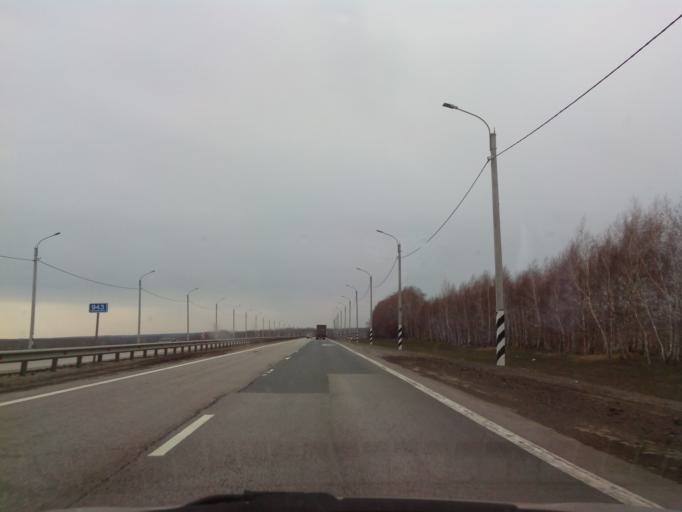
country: RU
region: Tambov
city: Selezni
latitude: 52.7410
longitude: 41.2185
